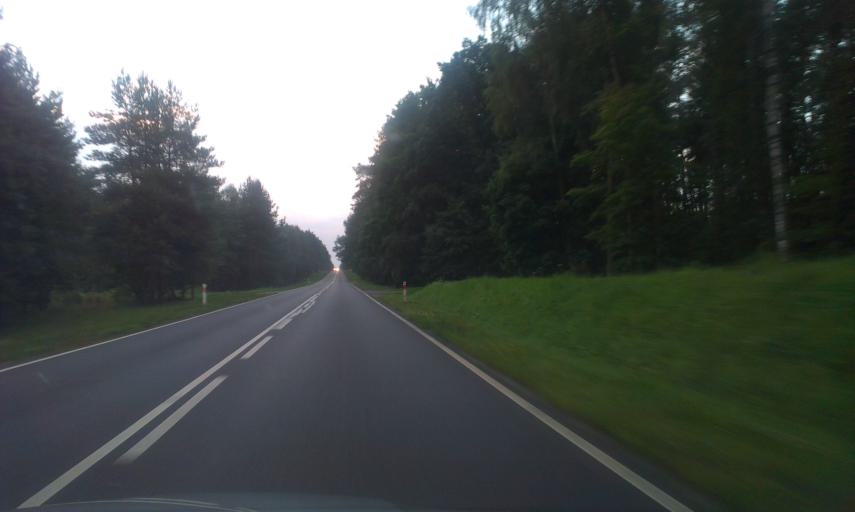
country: PL
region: West Pomeranian Voivodeship
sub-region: Powiat koszalinski
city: Sianow
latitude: 54.1152
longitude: 16.3212
